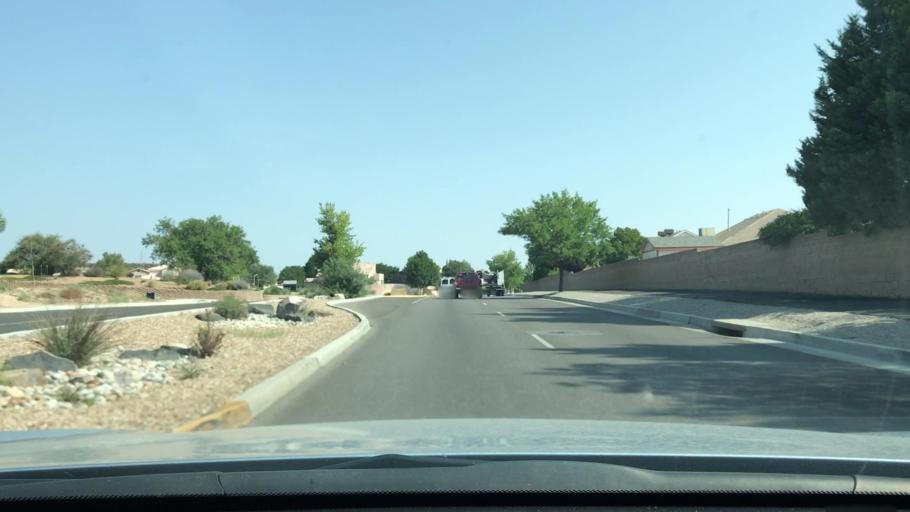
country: US
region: New Mexico
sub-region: Bernalillo County
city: Paradise Hills
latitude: 35.1818
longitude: -106.6874
